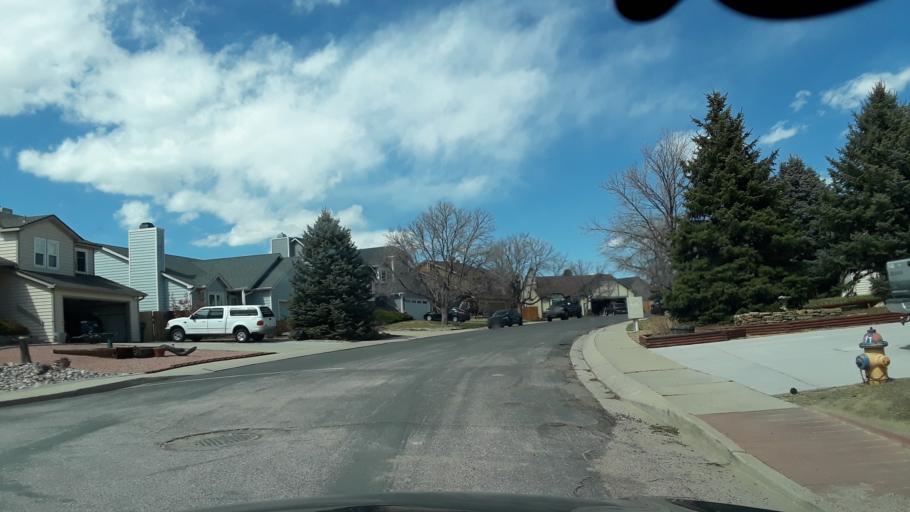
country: US
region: Colorado
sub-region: El Paso County
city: Black Forest
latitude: 38.9604
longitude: -104.7500
